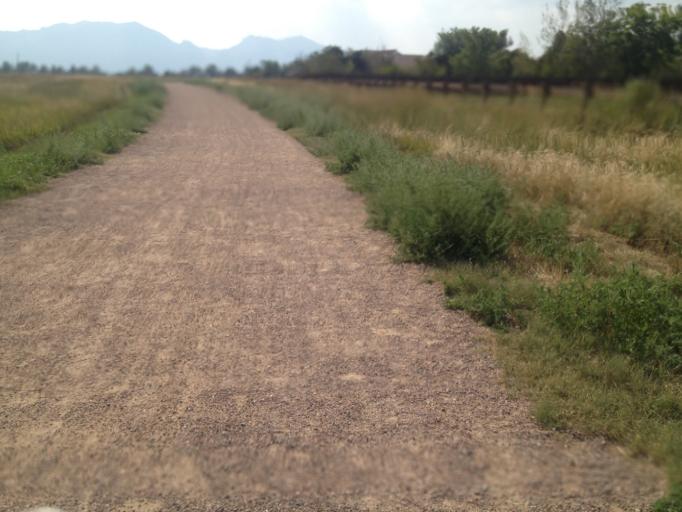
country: US
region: Colorado
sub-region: Boulder County
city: Superior
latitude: 39.9723
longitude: -105.1768
